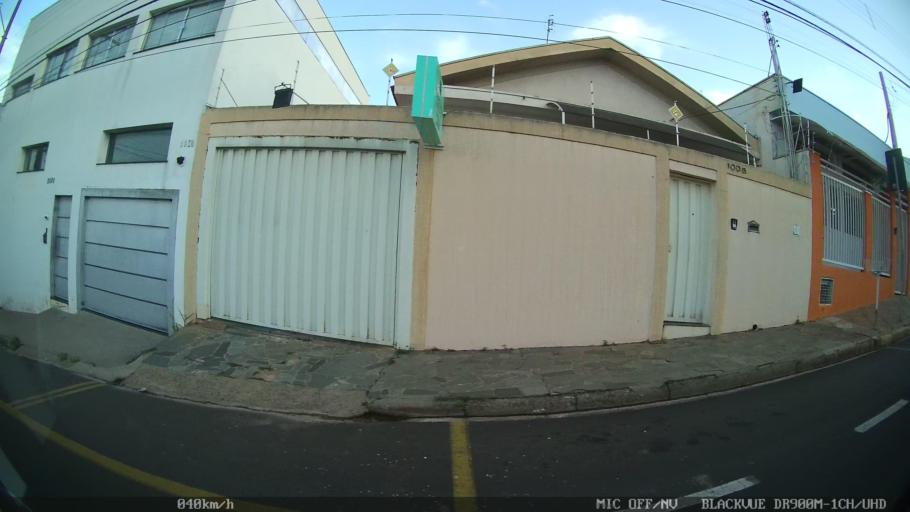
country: BR
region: Sao Paulo
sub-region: Franca
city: Franca
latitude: -20.5258
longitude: -47.4038
